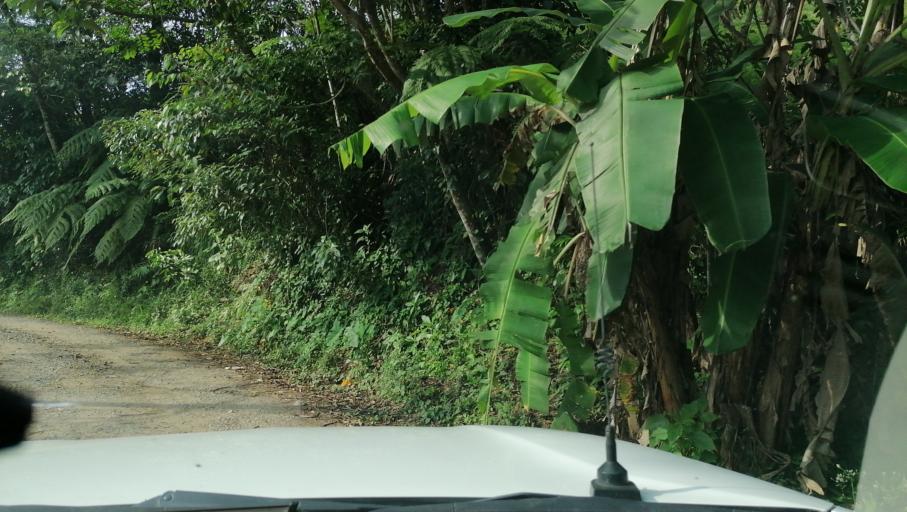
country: MX
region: Chiapas
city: Pichucalco
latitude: 17.4821
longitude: -93.2222
